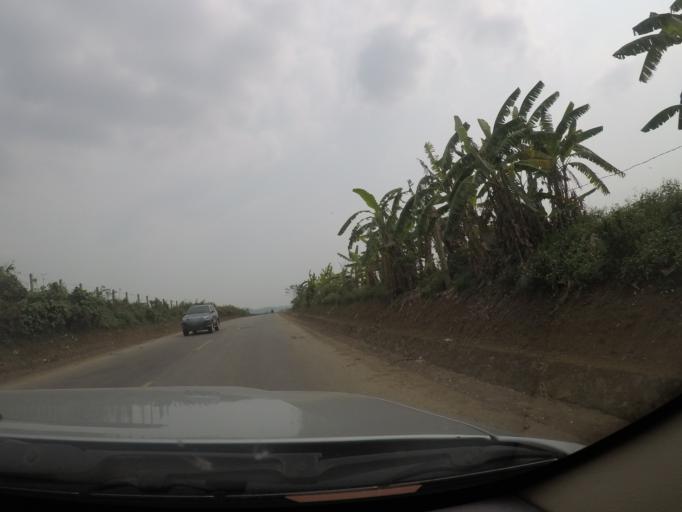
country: VN
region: Thanh Hoa
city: Thi Tran Ben Sung
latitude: 19.3818
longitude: 105.4613
